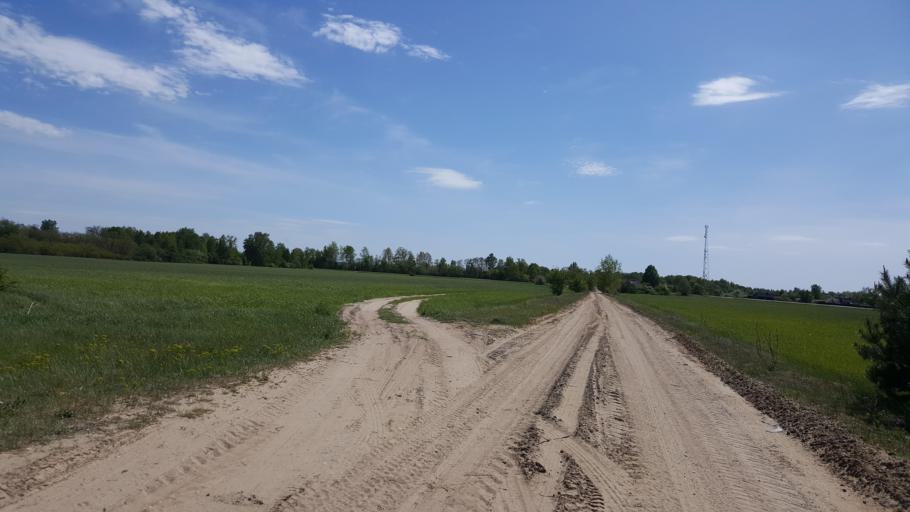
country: BY
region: Brest
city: Zhabinka
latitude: 52.3636
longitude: 24.1584
